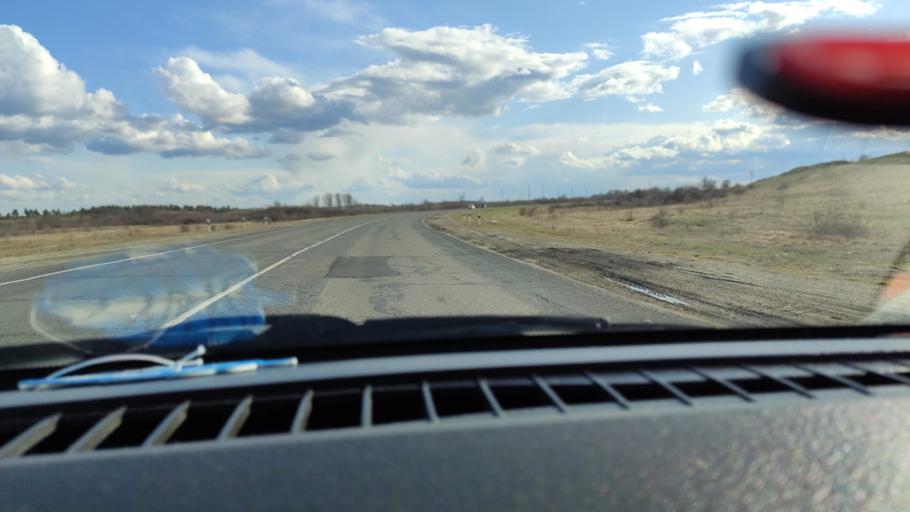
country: RU
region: Saratov
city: Sennoy
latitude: 52.0894
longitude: 46.8083
